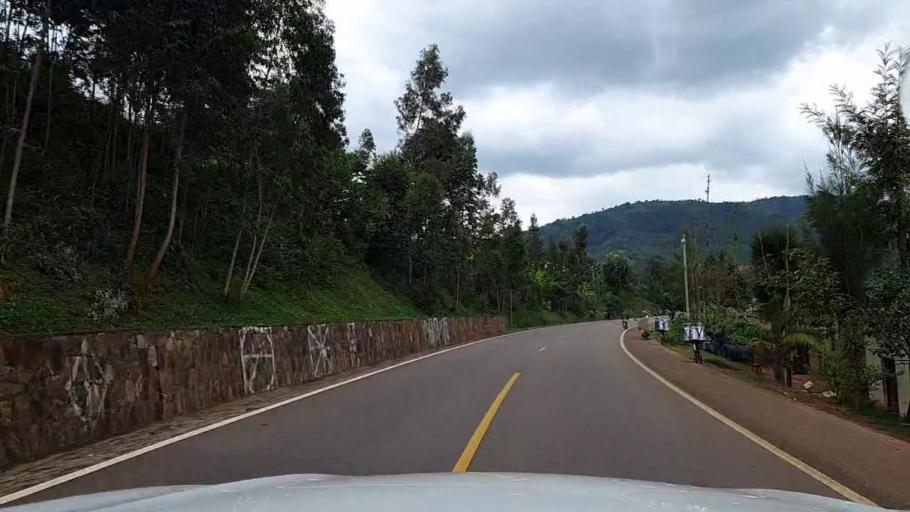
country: RW
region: Northern Province
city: Byumba
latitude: -1.6801
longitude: 30.1008
